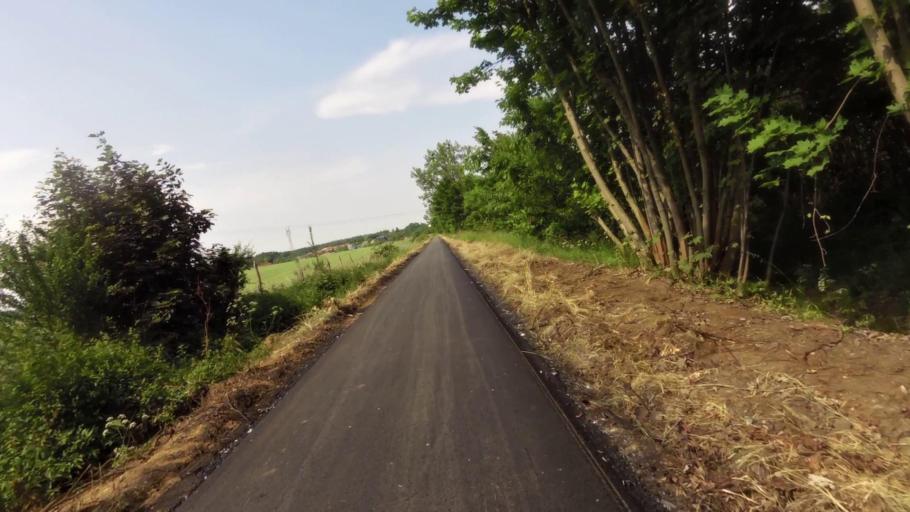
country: PL
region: West Pomeranian Voivodeship
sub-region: Powiat pyrzycki
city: Bielice
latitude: 53.2110
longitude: 14.6122
